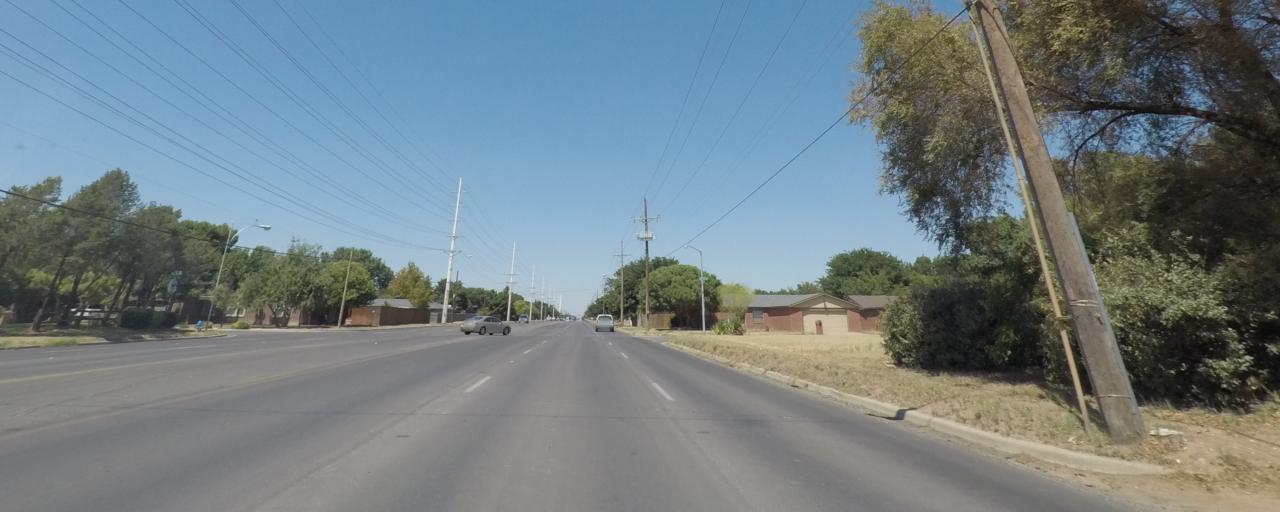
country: US
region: Texas
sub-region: Lubbock County
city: Lubbock
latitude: 33.5119
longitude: -101.8876
